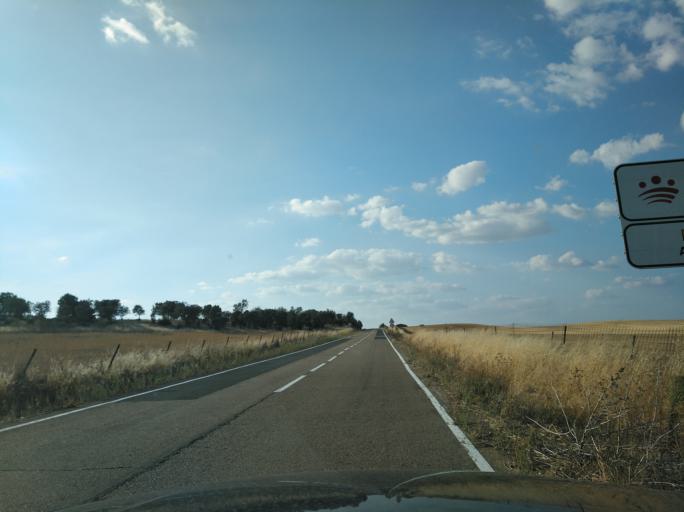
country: PT
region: Portalegre
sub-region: Campo Maior
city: Campo Maior
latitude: 39.1199
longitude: -7.0572
